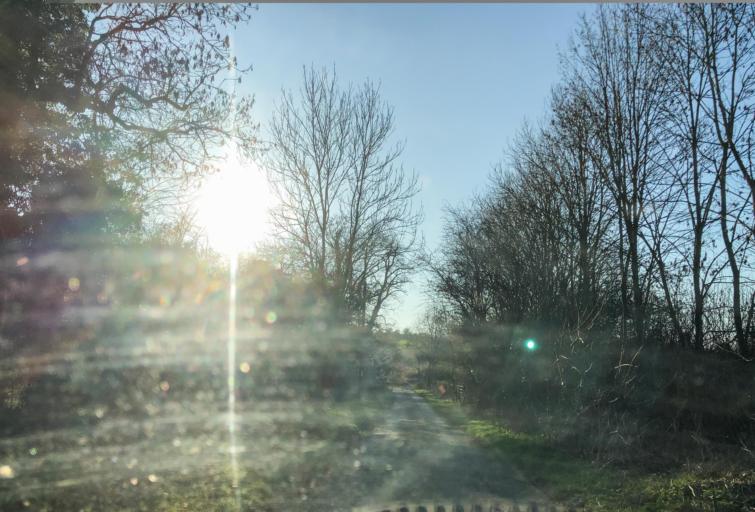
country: GB
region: England
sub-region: Warwickshire
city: Harbury
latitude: 52.1999
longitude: -1.5108
